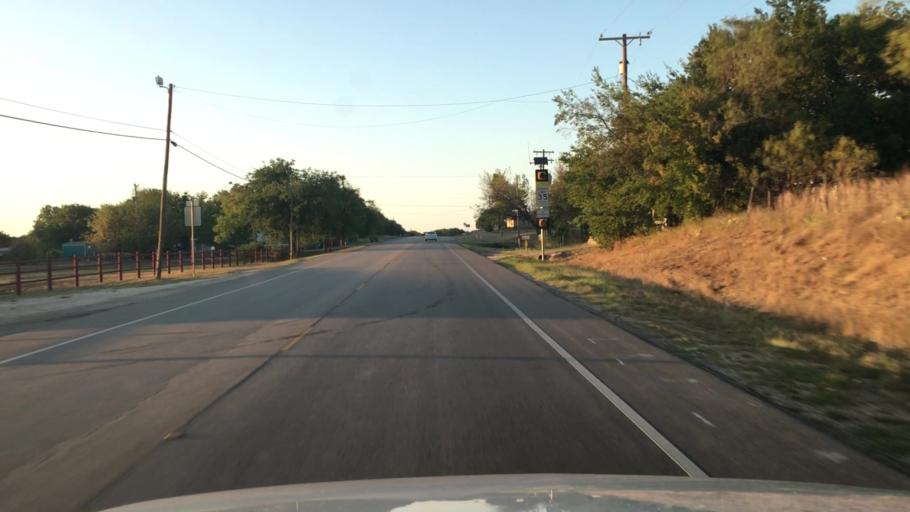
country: US
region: Texas
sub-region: Hamilton County
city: Hico
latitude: 31.9902
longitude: -98.0264
